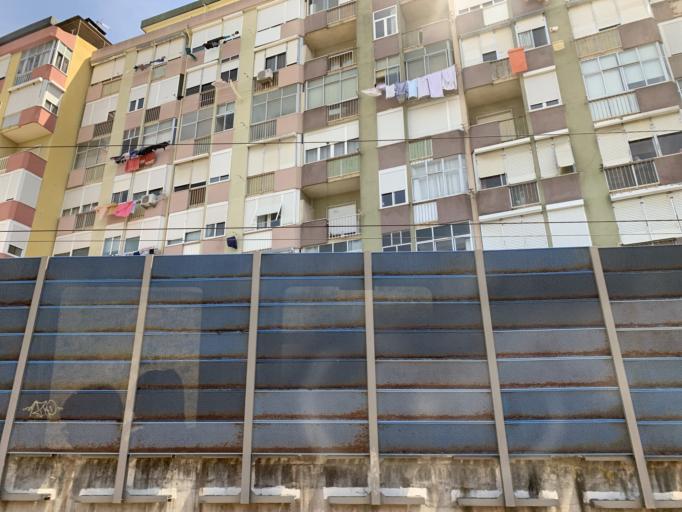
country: PT
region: Lisbon
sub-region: Amadora
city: Amadora
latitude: 38.7555
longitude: -9.2281
